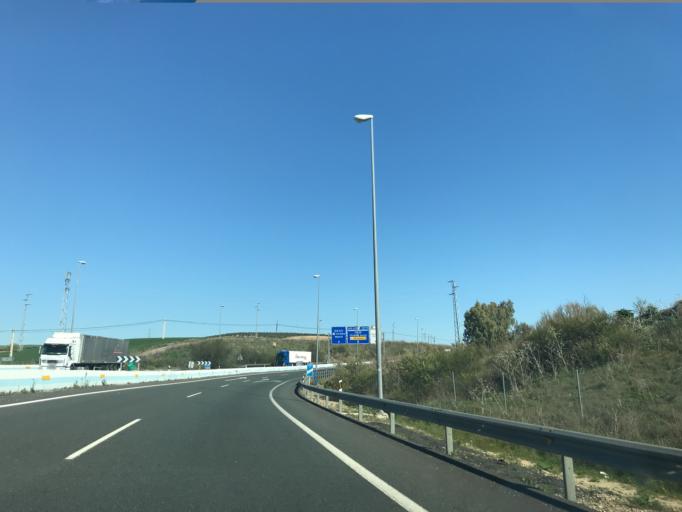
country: ES
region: Andalusia
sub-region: Province of Cordoba
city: Cordoba
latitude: 37.8164
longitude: -4.7973
